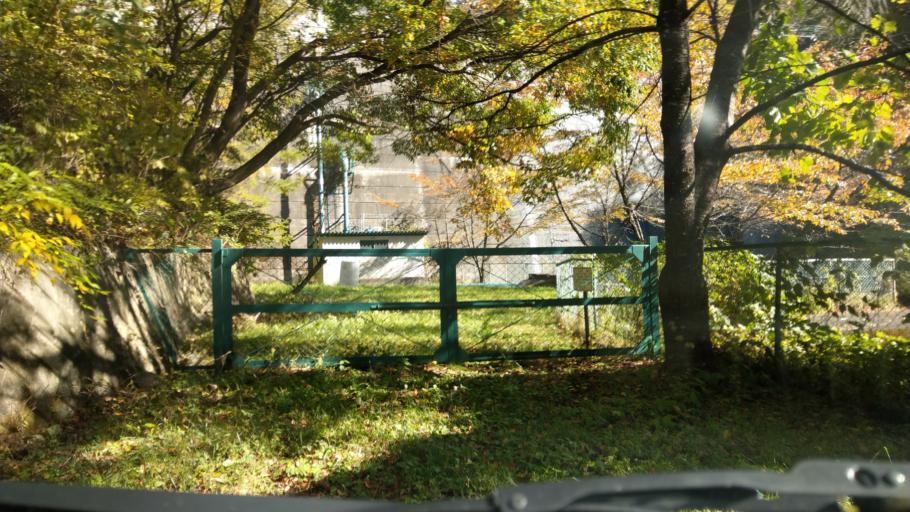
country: JP
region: Nagano
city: Komoro
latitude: 36.3745
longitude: 138.4246
